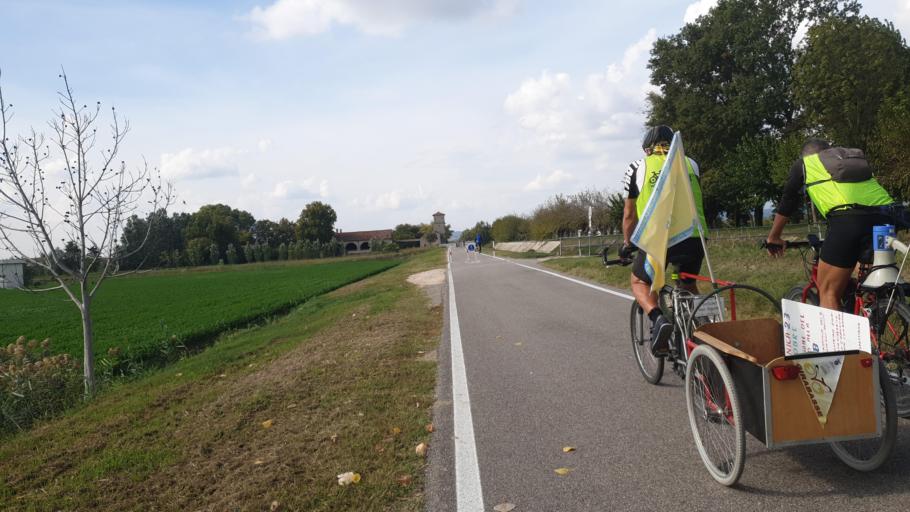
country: IT
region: Veneto
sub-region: Provincia di Vicenza
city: Agugliaro
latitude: 45.3295
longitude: 11.5772
